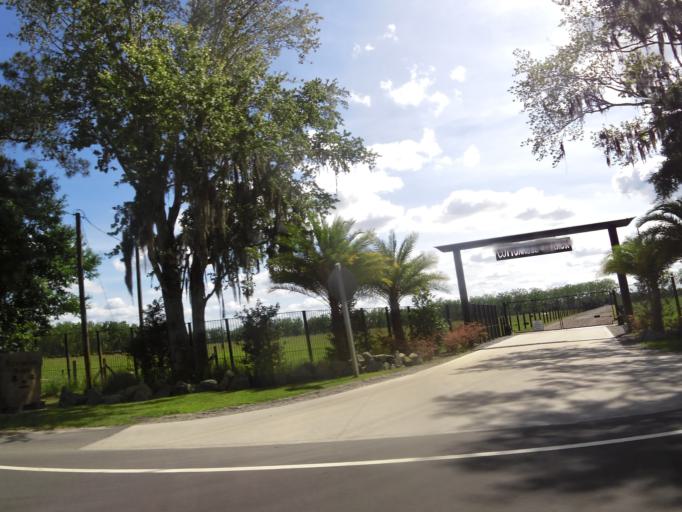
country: US
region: Florida
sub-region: Nassau County
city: Callahan
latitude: 30.6110
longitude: -81.8761
